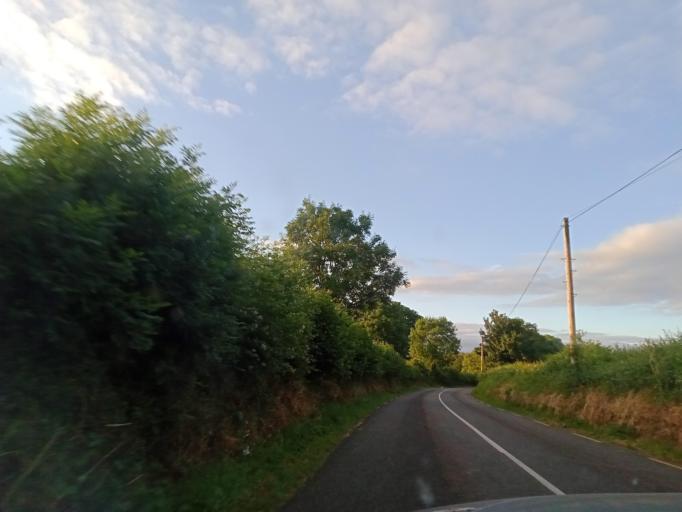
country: IE
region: Leinster
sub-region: Kilkenny
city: Castlecomer
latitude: 52.8482
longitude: -7.1777
